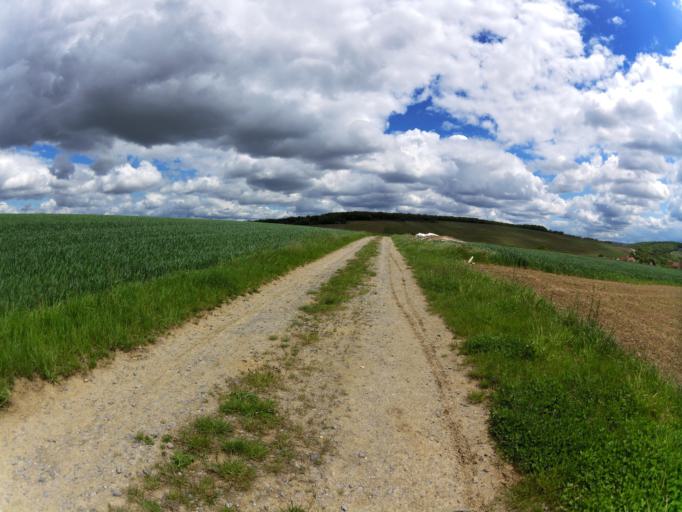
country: DE
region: Bavaria
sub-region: Regierungsbezirk Unterfranken
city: Volkach
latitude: 49.8760
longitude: 10.2490
